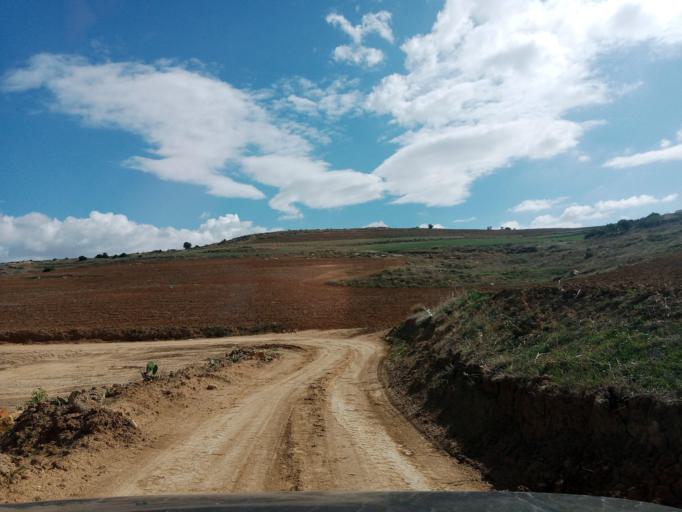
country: TN
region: Tunis
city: Oued Lill
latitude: 36.8136
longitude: 9.9976
